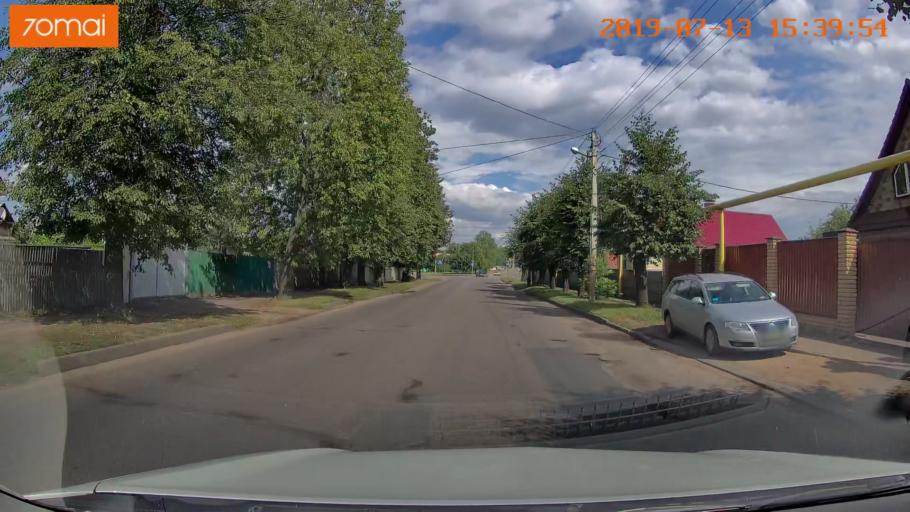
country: BY
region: Mogilev
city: Babruysk
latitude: 53.1349
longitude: 29.1872
